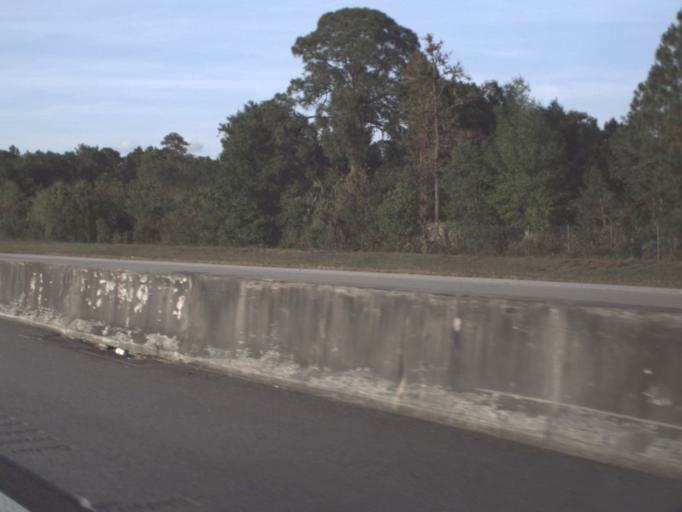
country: US
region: Florida
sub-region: Brevard County
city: Sharpes
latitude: 28.4160
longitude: -80.8202
